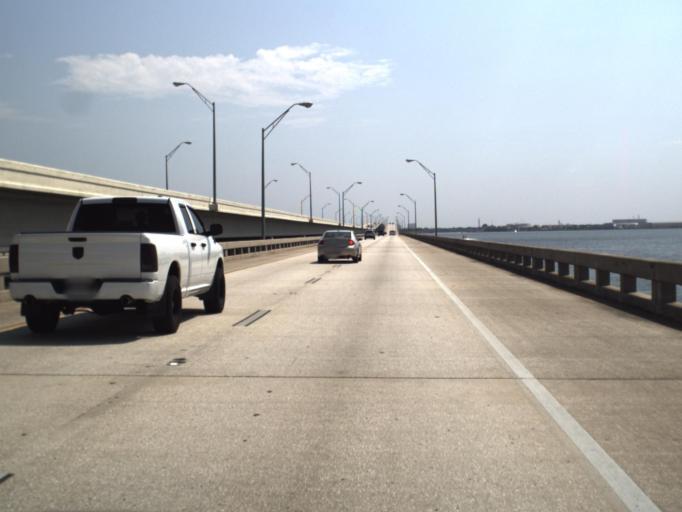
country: US
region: Florida
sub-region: Pinellas County
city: Gandy
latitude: 27.8843
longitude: -82.5642
